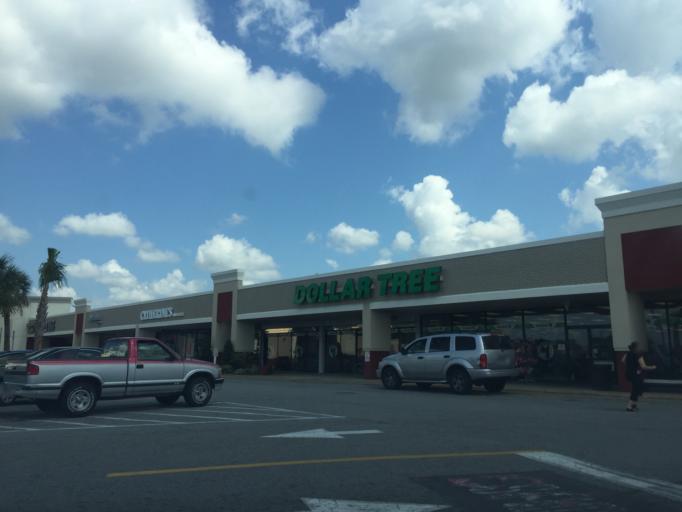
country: US
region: Georgia
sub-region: Chatham County
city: Isle of Hope
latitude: 32.0065
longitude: -81.1169
